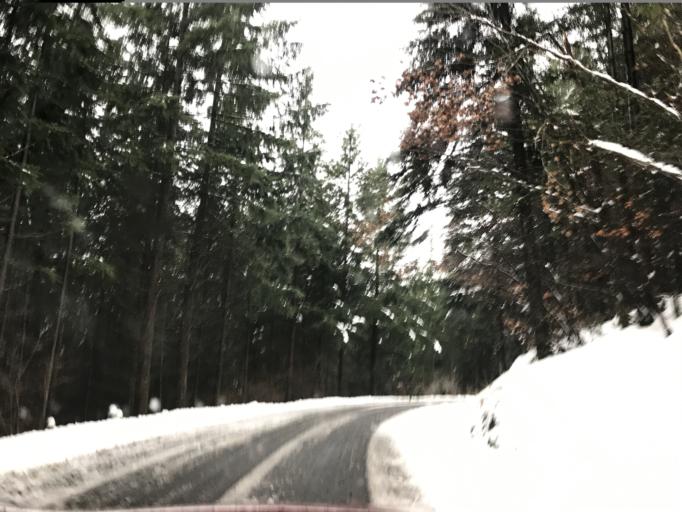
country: FR
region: Auvergne
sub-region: Departement du Puy-de-Dome
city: Celles-sur-Durolle
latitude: 45.7508
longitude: 3.6711
